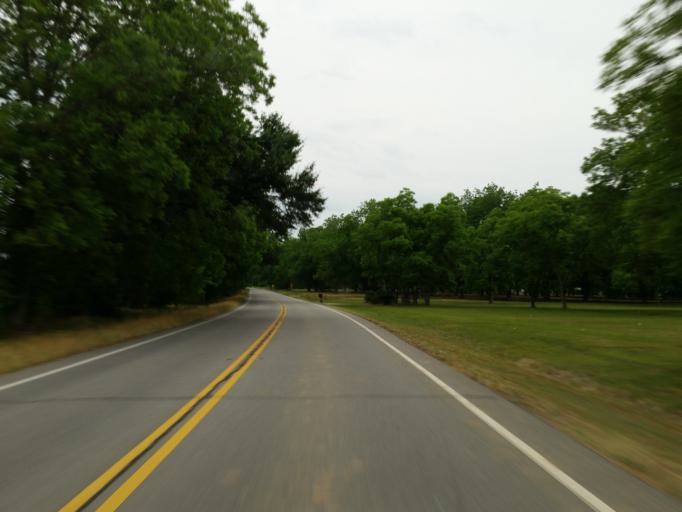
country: US
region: Georgia
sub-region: Dooly County
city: Vienna
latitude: 32.1490
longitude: -83.7987
